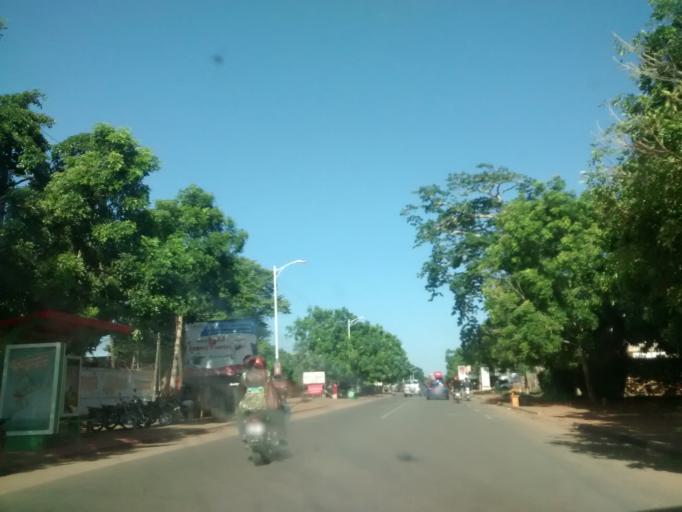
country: TG
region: Maritime
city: Lome
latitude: 6.1720
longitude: 1.1890
